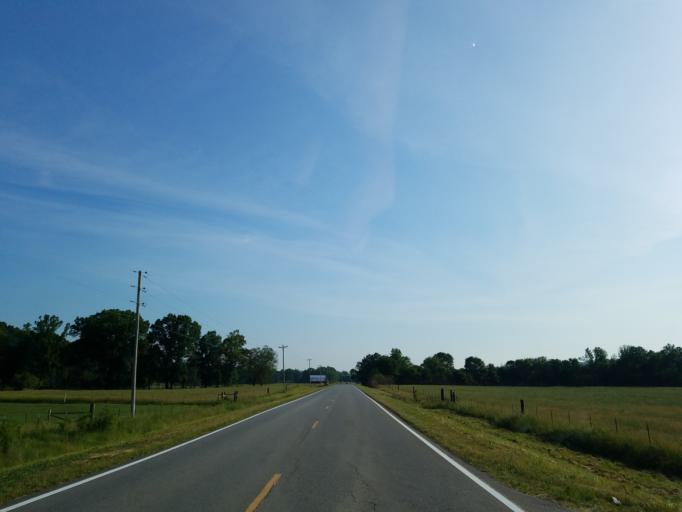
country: US
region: Georgia
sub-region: Chattooga County
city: Trion
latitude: 34.5043
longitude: -85.2418
